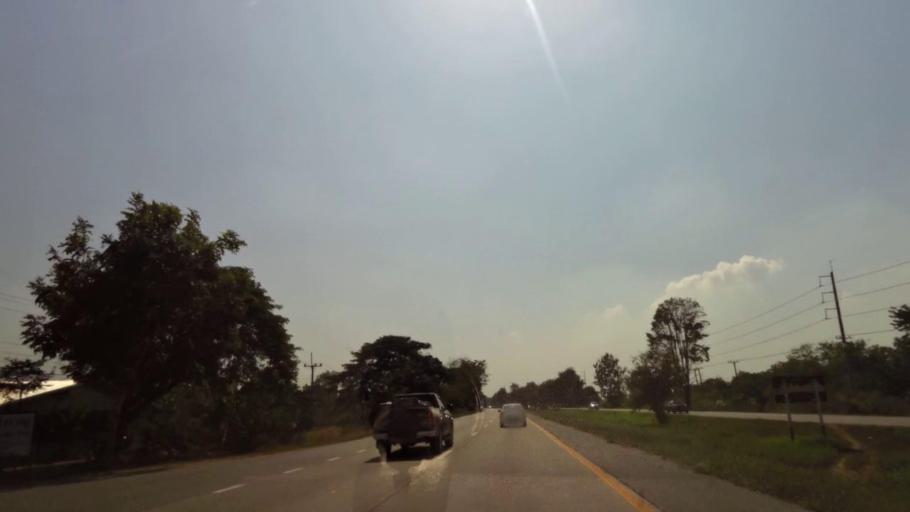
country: TH
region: Phichit
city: Wachira Barami
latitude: 16.5893
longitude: 100.1469
